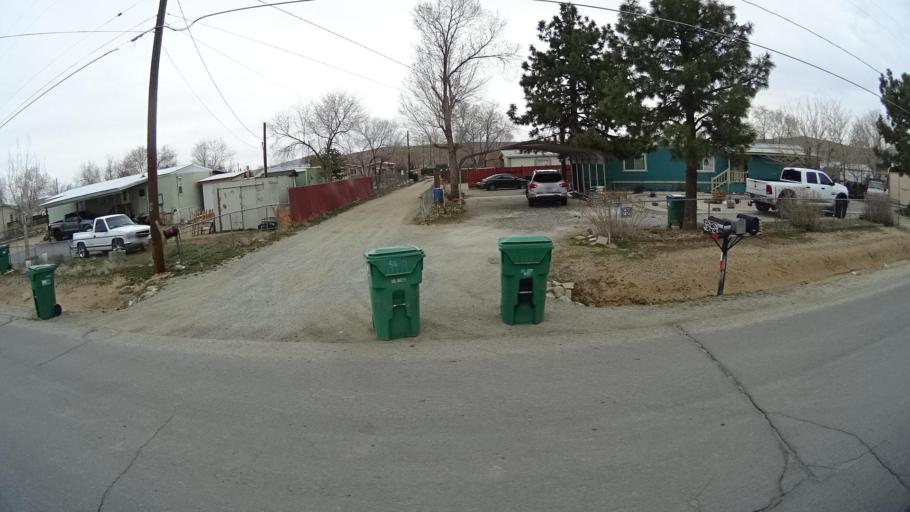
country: US
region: Nevada
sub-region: Washoe County
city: Sun Valley
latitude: 39.5991
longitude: -119.7711
